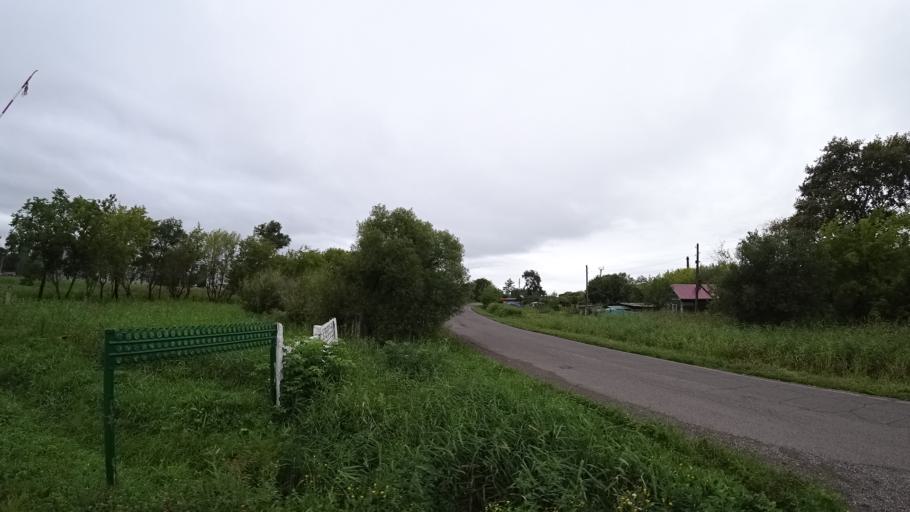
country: RU
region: Primorskiy
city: Chernigovka
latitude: 44.3328
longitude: 132.5321
